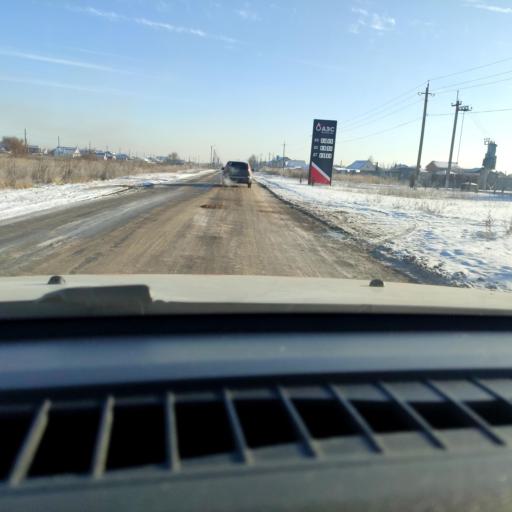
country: RU
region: Samara
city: Podstepki
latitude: 53.5230
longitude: 49.1463
